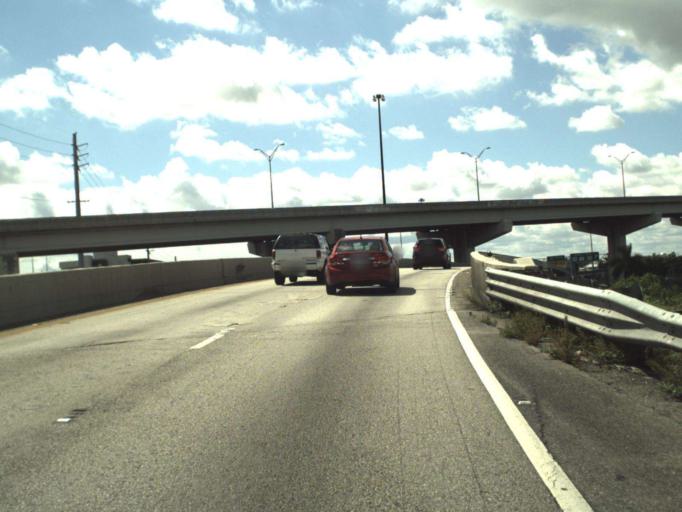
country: US
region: Florida
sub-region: Miami-Dade County
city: Norland
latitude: 25.9322
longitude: -80.2050
